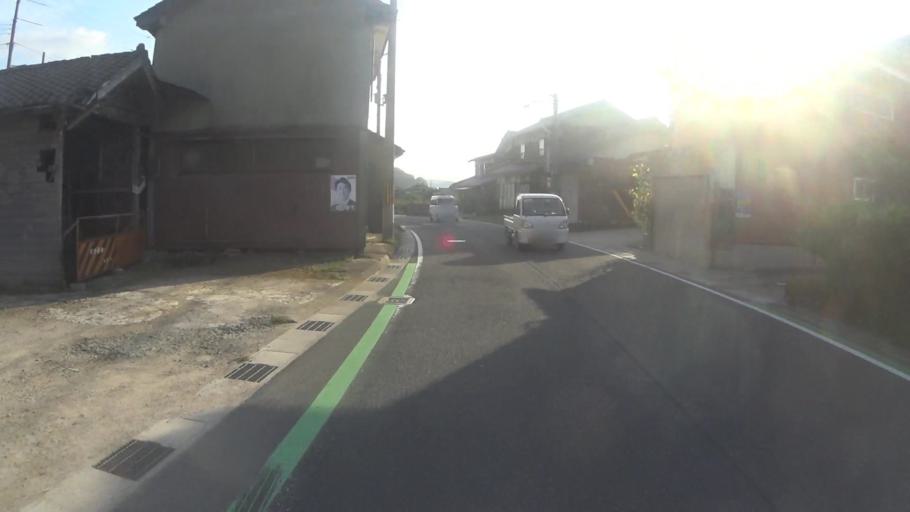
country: JP
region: Kyoto
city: Miyazu
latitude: 35.6759
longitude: 135.0966
